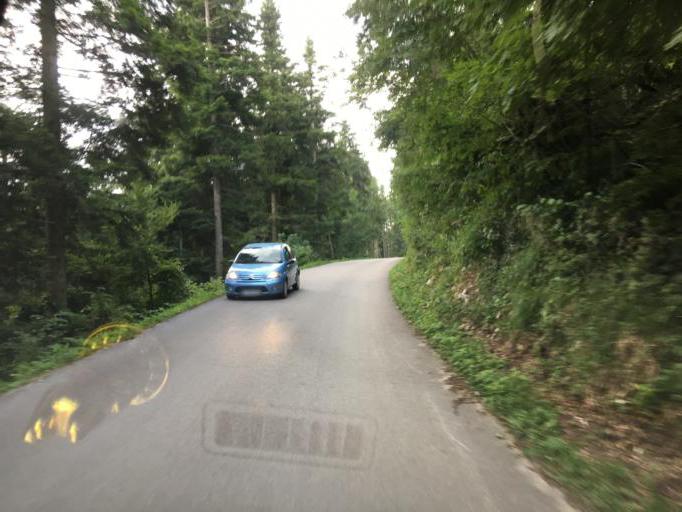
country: SI
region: Postojna
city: Postojna
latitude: 45.7985
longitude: 14.2010
